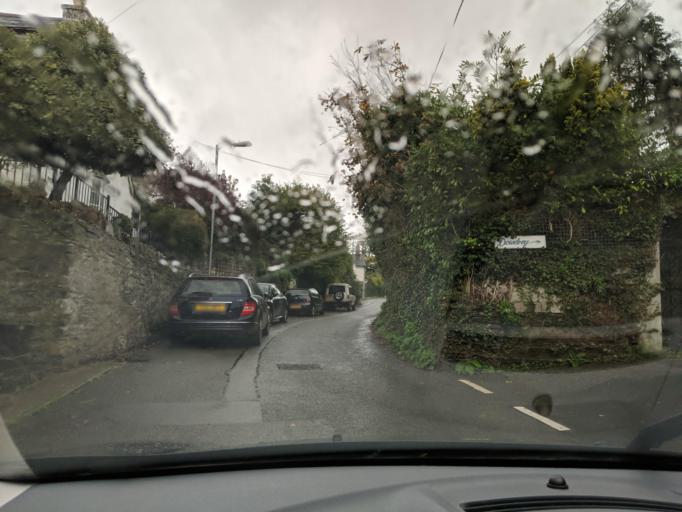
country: GB
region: England
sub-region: Cornwall
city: Wadebridge
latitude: 50.5142
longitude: -4.8213
